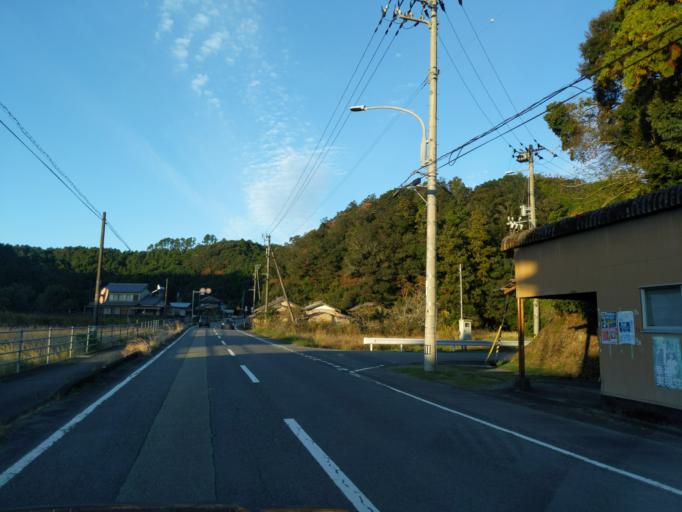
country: JP
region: Kochi
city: Muroto-misakicho
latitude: 33.6250
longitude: 134.3566
